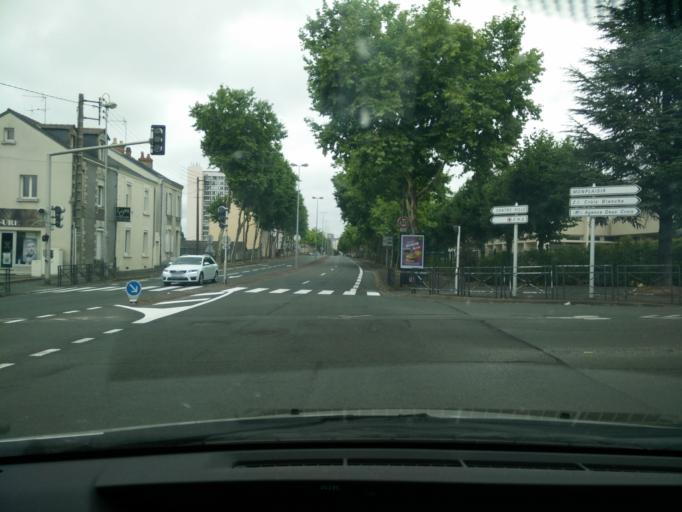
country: FR
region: Pays de la Loire
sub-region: Departement de Maine-et-Loire
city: Angers
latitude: 47.4690
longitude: -0.5319
